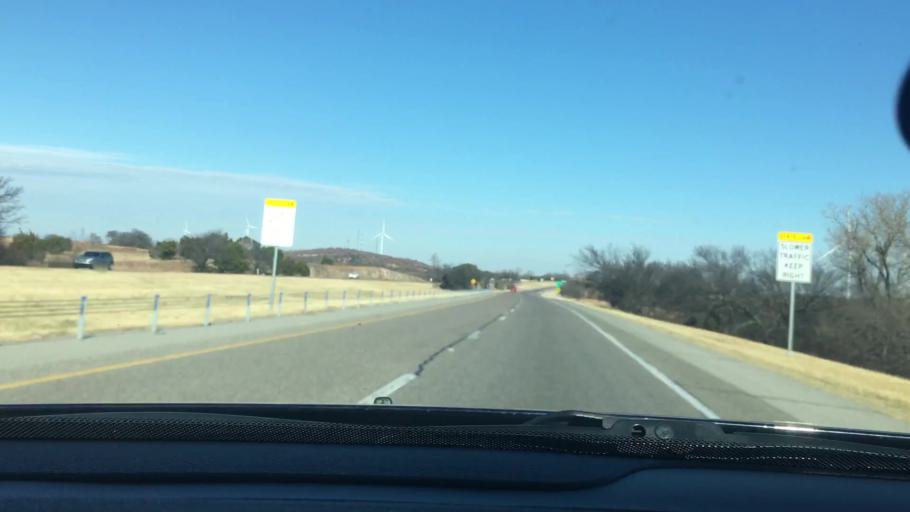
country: US
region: Oklahoma
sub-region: Murray County
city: Davis
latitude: 34.3891
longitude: -97.1415
